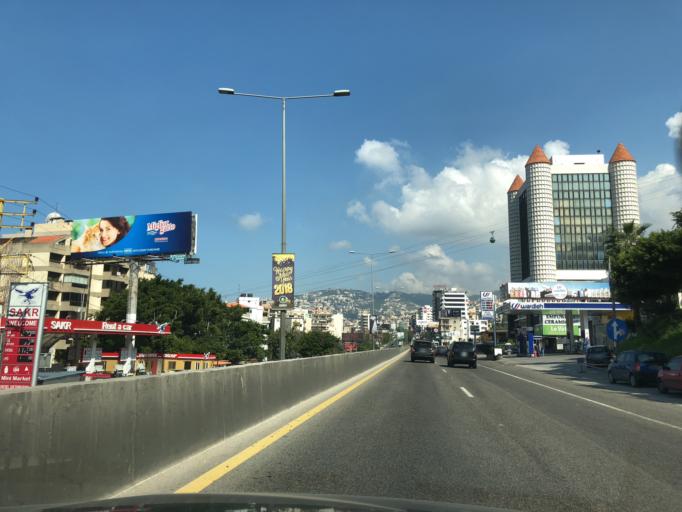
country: LB
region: Mont-Liban
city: Djounie
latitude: 33.9894
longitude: 35.6421
